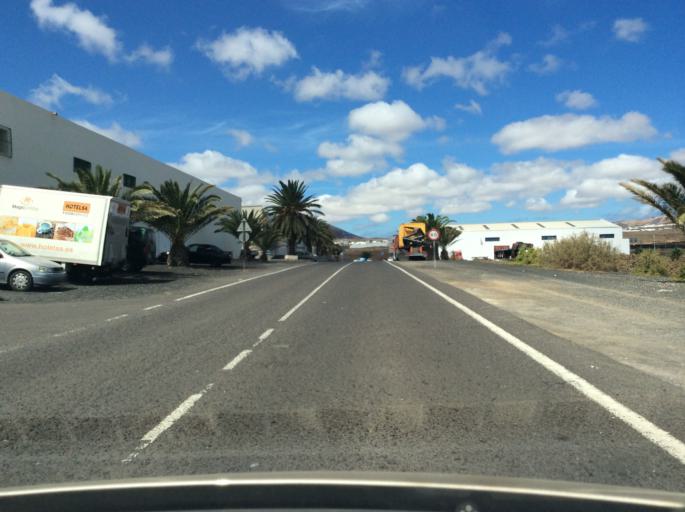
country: ES
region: Canary Islands
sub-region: Provincia de Las Palmas
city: Arrecife
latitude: 28.9734
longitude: -13.5325
